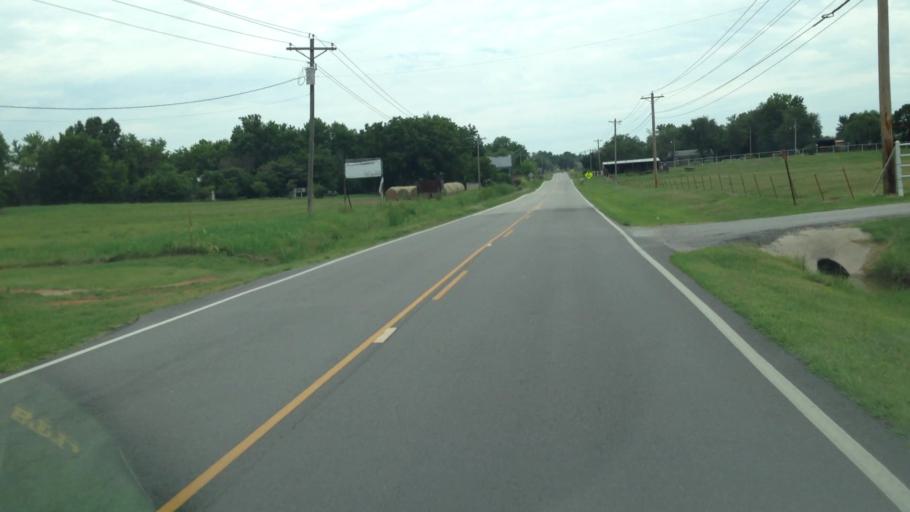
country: US
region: Oklahoma
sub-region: Delaware County
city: Cleora
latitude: 36.5752
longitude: -94.9707
